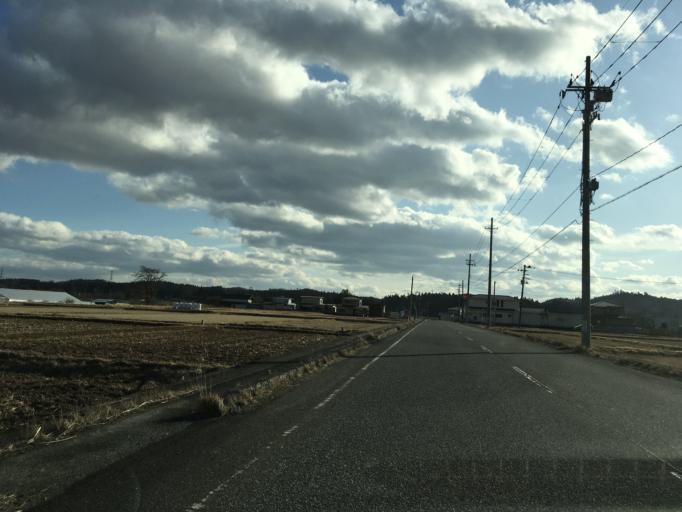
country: JP
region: Iwate
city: Ichinoseki
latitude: 38.8291
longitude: 140.9990
